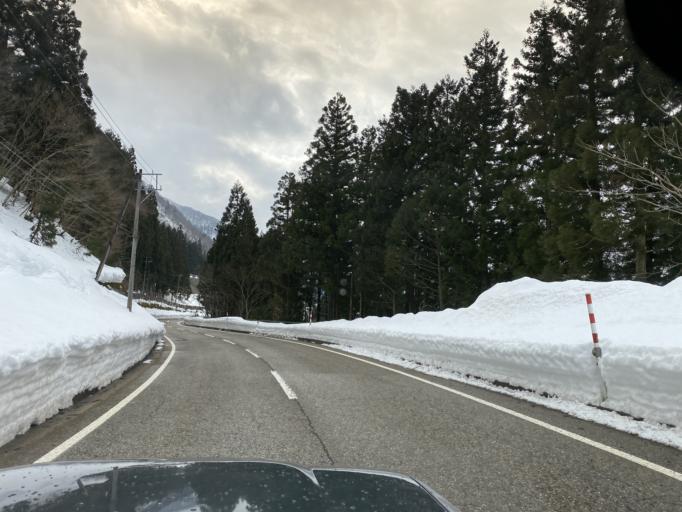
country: JP
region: Toyama
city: Fukumitsu
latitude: 36.3987
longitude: 136.8798
